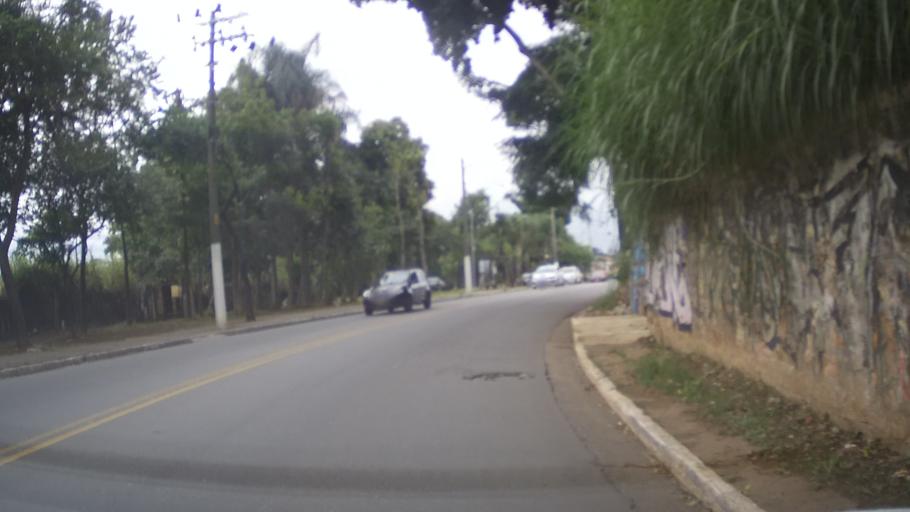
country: BR
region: Sao Paulo
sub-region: Guarulhos
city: Guarulhos
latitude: -23.4688
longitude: -46.5962
